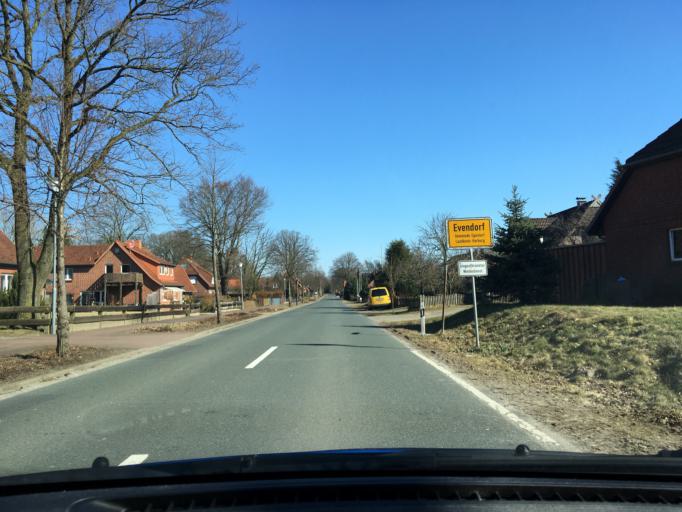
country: DE
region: Lower Saxony
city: Egestorf
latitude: 53.1475
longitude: 10.0613
